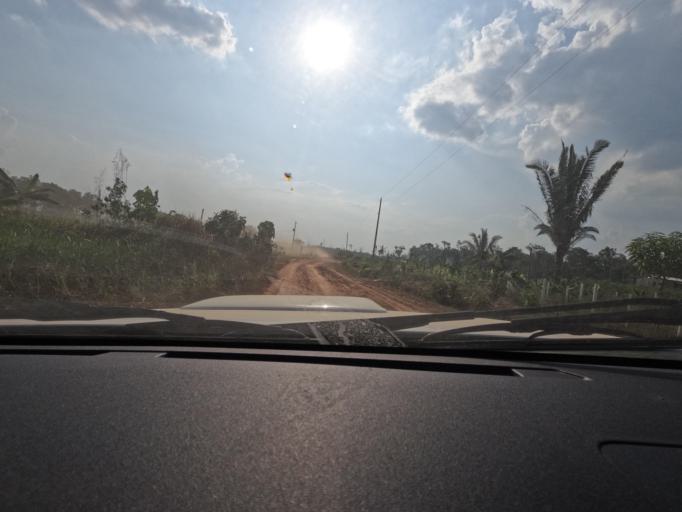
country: BR
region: Rondonia
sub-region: Porto Velho
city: Porto Velho
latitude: -8.5741
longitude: -64.0057
